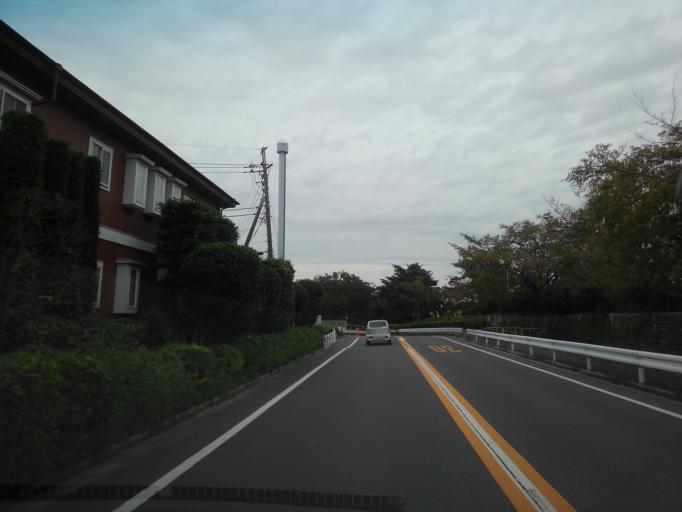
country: JP
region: Tokyo
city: Higashimurayama-shi
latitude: 35.7668
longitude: 139.4434
